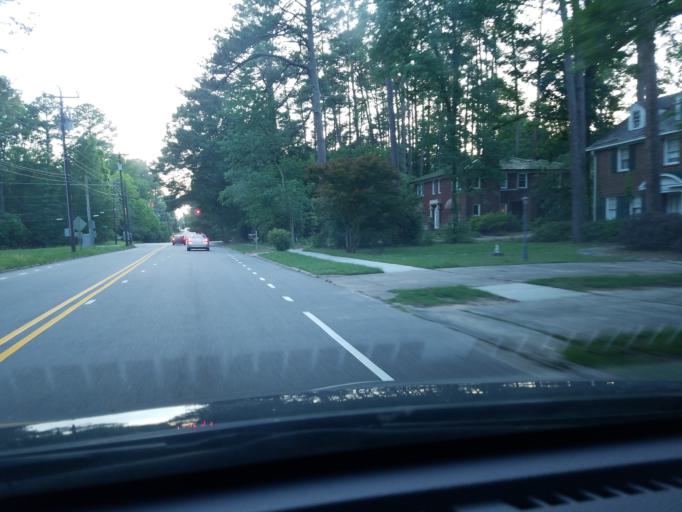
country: US
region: North Carolina
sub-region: Durham County
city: Durham
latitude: 35.9713
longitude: -78.9278
